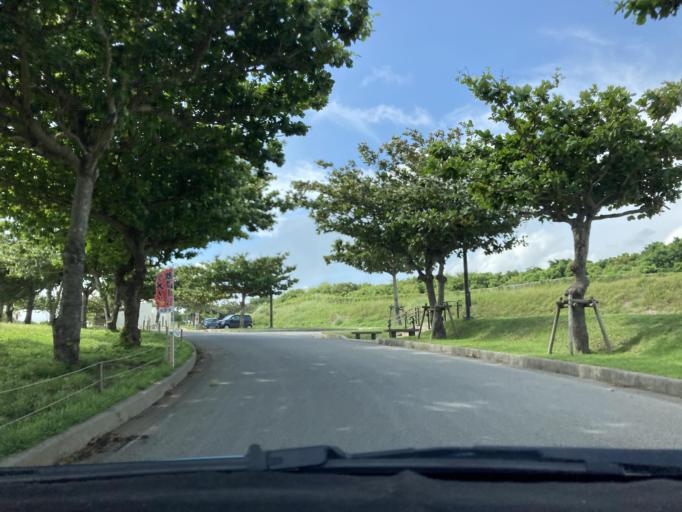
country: JP
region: Okinawa
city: Itoman
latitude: 26.0990
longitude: 127.7259
